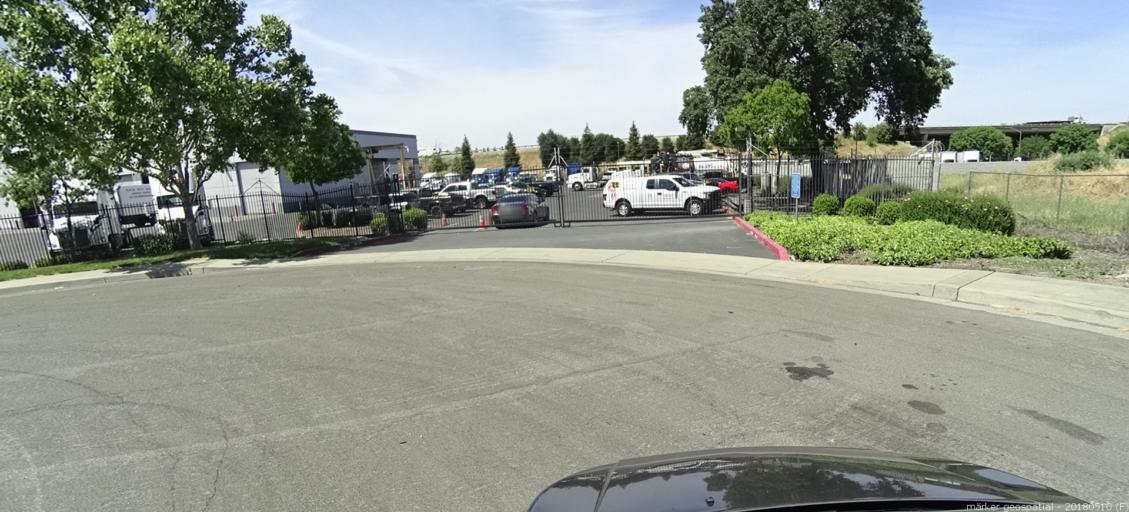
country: US
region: California
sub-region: Sacramento County
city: Rio Linda
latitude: 38.6395
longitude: -121.4488
